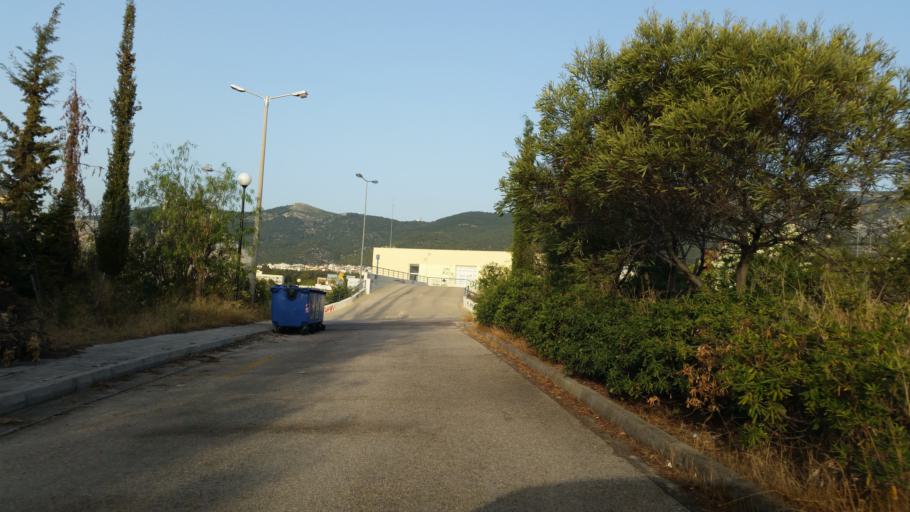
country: GR
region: Attica
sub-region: Nomos Attikis
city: Zografos
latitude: 37.9773
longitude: 23.7771
